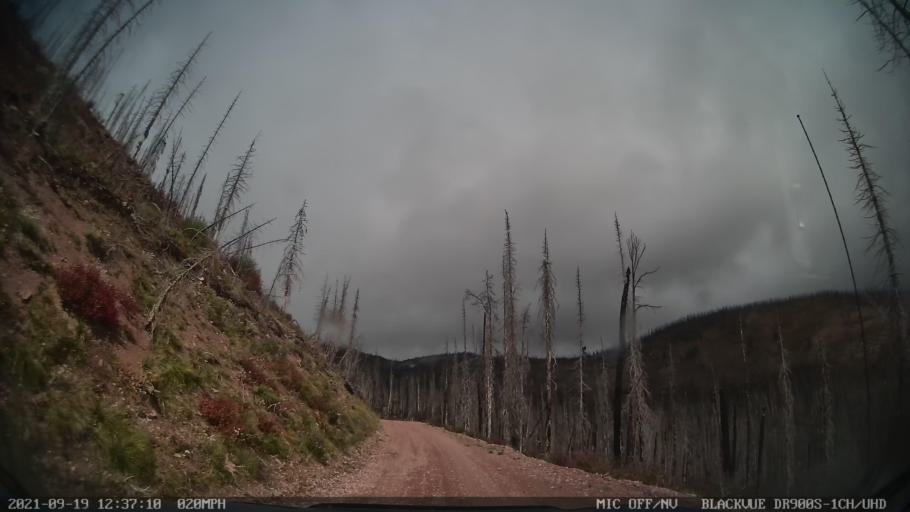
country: US
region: Montana
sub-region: Missoula County
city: Seeley Lake
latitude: 47.1907
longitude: -113.3449
